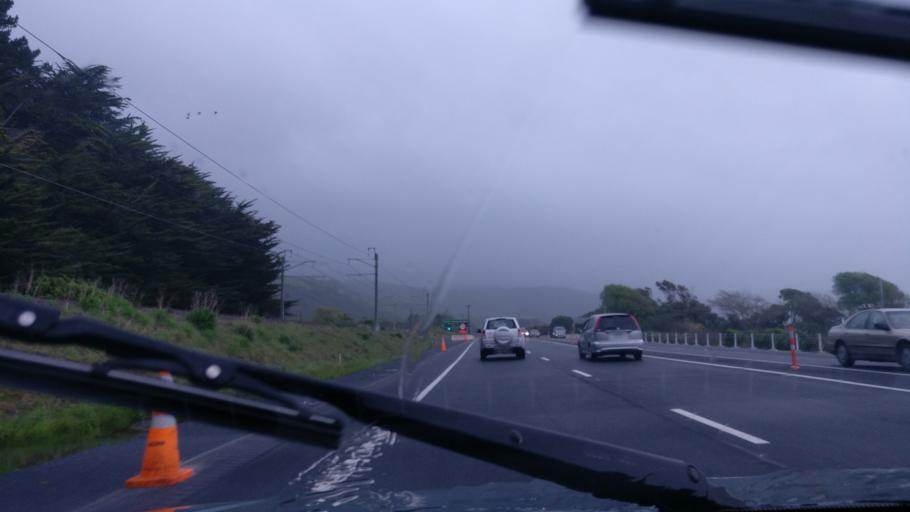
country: NZ
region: Wellington
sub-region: Kapiti Coast District
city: Paraparaumu
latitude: -40.9543
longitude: 174.9886
